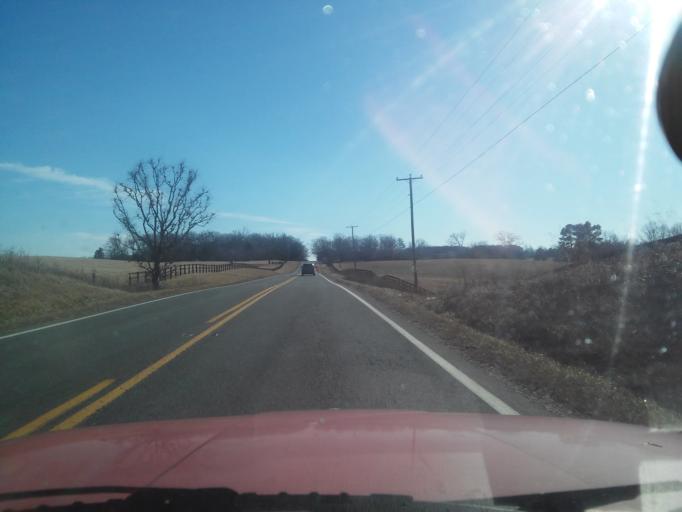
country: US
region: Virginia
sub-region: Orange County
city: Gordonsville
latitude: 38.0183
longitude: -78.1910
